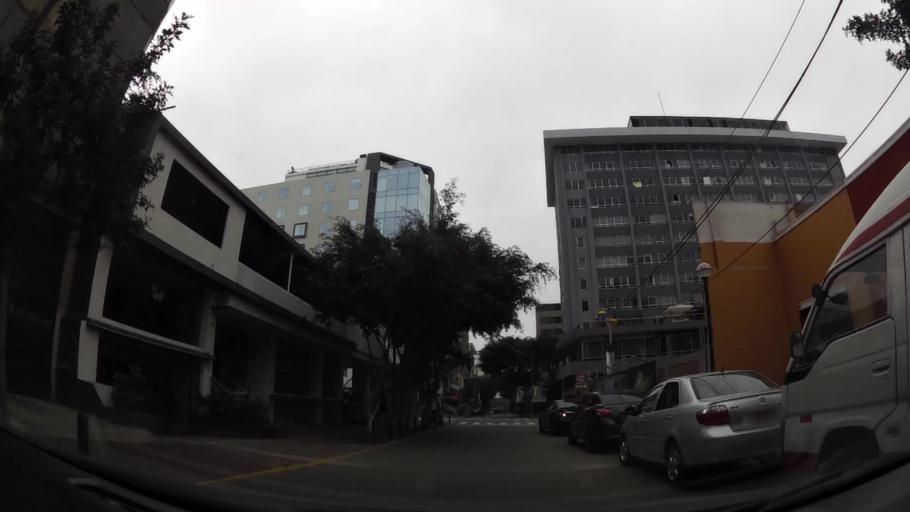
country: PE
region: Lima
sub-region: Lima
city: San Isidro
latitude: -12.1229
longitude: -77.0279
